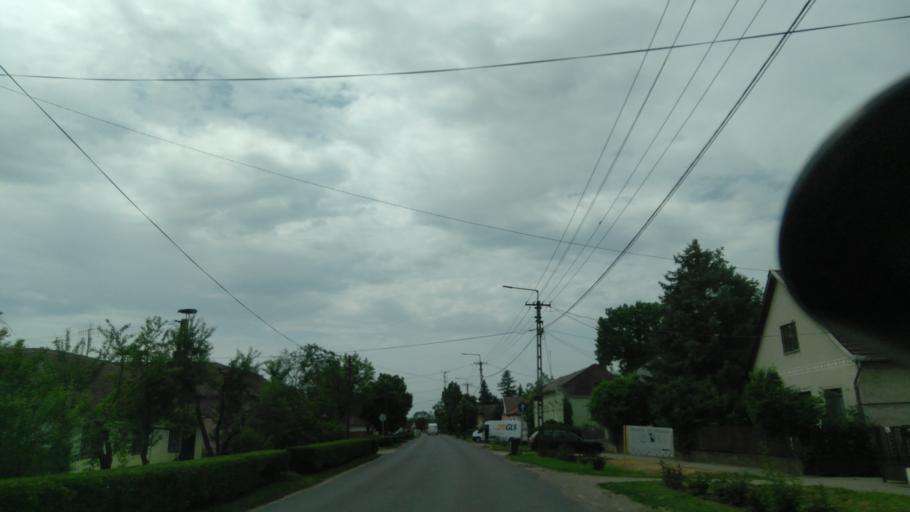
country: HU
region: Bekes
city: Fuzesgyarmat
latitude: 47.1062
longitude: 21.2106
